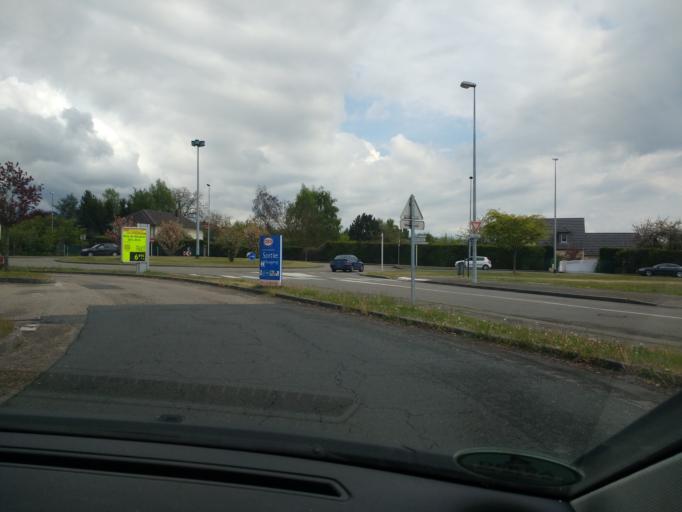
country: FR
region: Lorraine
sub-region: Departement de la Moselle
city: Sarreguemines
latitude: 49.1159
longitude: 7.0940
